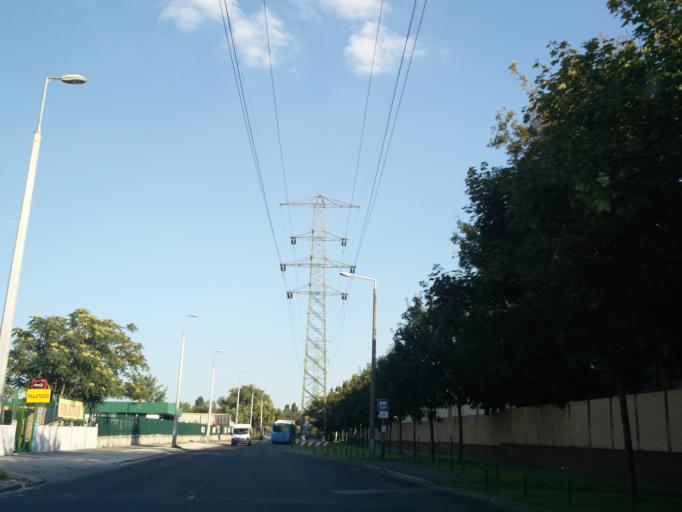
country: HU
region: Budapest
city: Budapest XIX. keruelet
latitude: 47.4706
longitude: 19.1265
